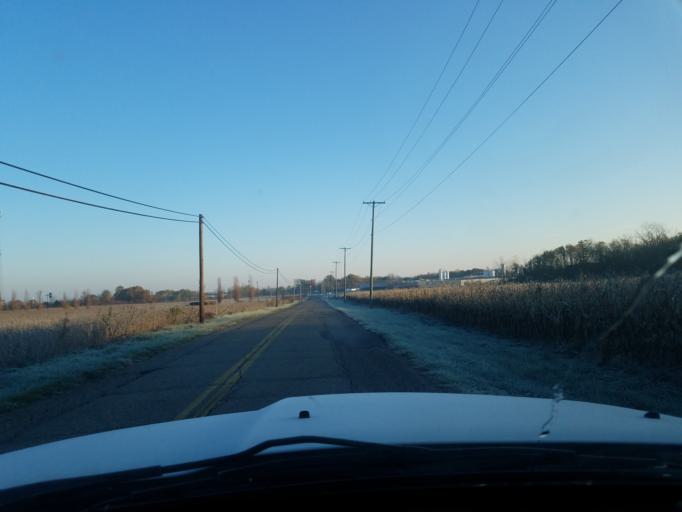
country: US
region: Indiana
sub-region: Montgomery County
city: Crawfordsville
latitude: 40.0688
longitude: -86.9021
